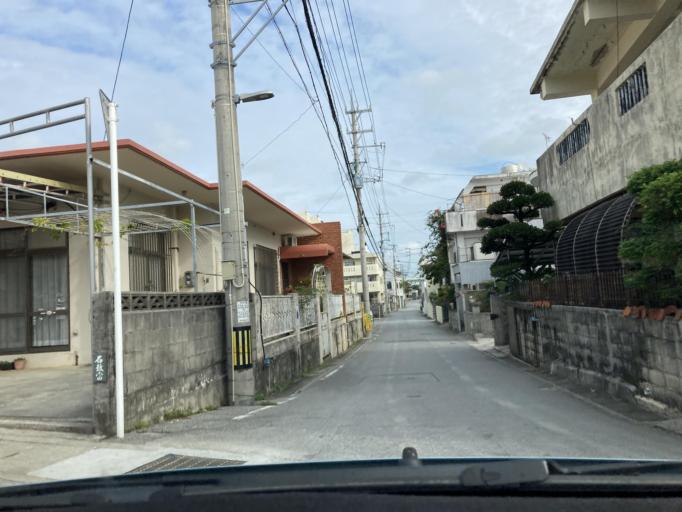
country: JP
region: Okinawa
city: Ginowan
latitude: 26.2059
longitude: 127.7538
